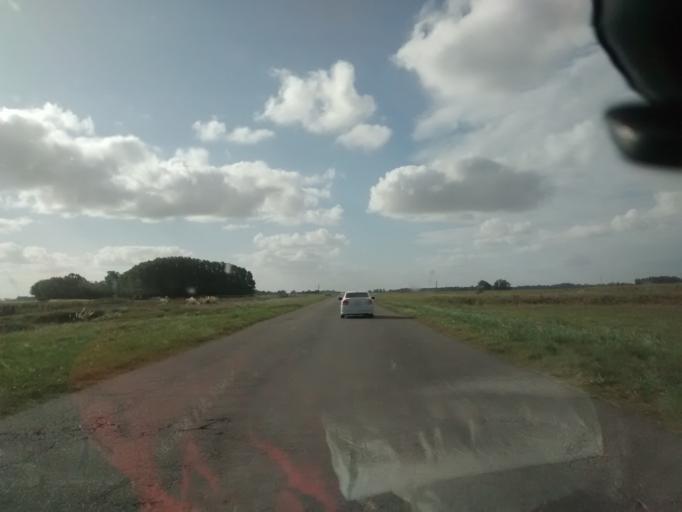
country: AR
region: Buenos Aires
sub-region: Partido de Ayacucho
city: Ayacucho
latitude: -37.2034
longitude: -58.5054
